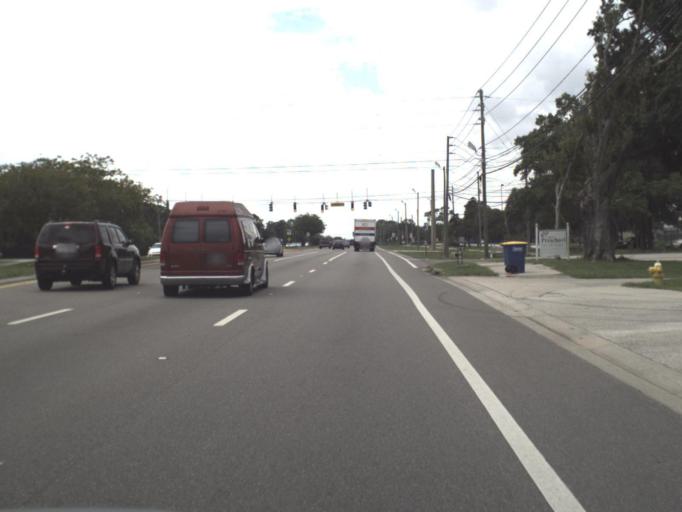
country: US
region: Florida
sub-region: Pinellas County
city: Saint George
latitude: 28.0352
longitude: -82.7092
